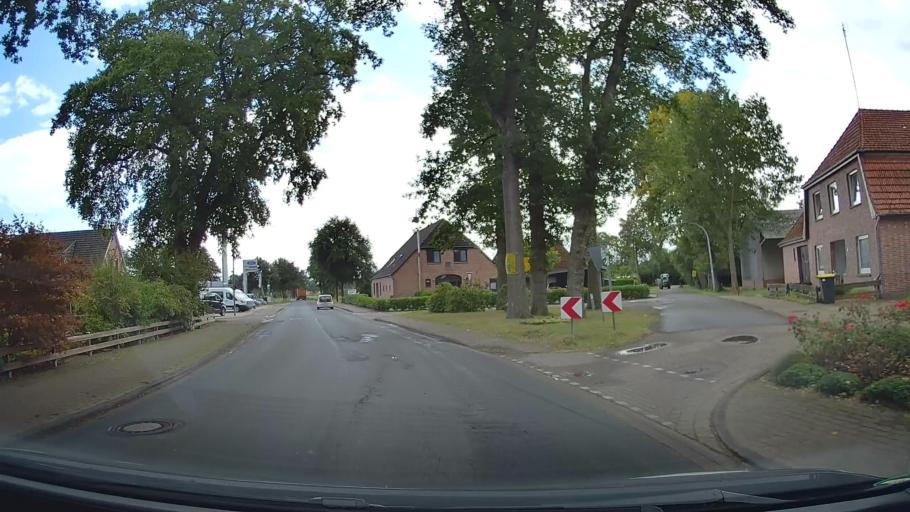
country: DE
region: Lower Saxony
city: Rhade
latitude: 53.3277
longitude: 9.1167
